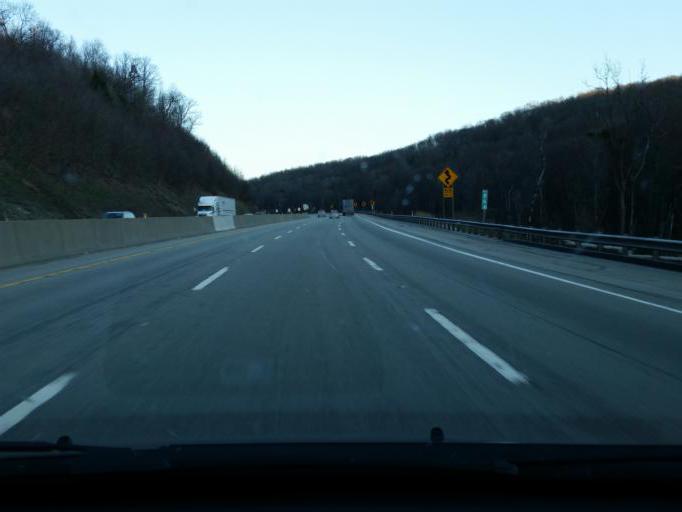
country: US
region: Pennsylvania
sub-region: Fayette County
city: Bear Rocks
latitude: 40.1515
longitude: -79.4301
